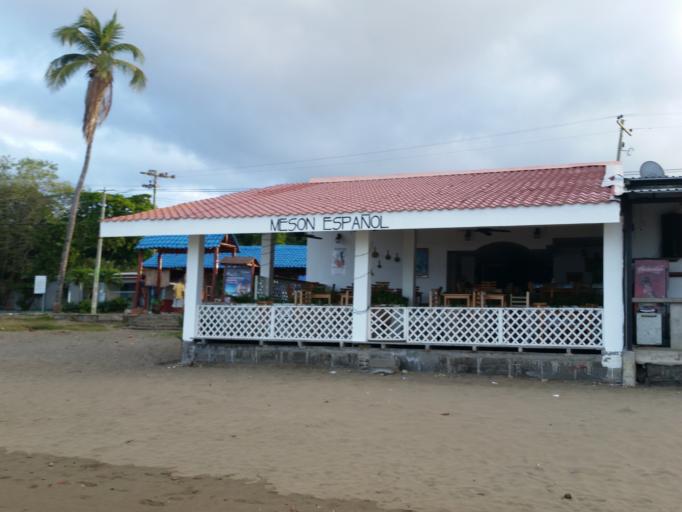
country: NI
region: Rivas
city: San Juan del Sur
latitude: 11.2558
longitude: -85.8730
